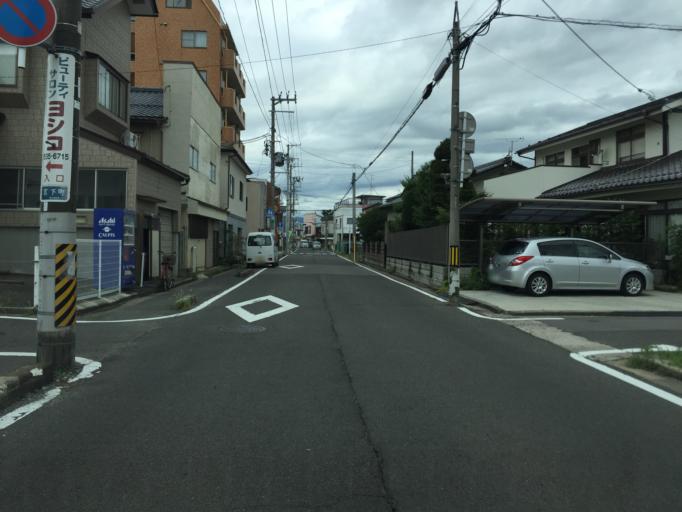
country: JP
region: Fukushima
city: Fukushima-shi
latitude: 37.7601
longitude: 140.4666
